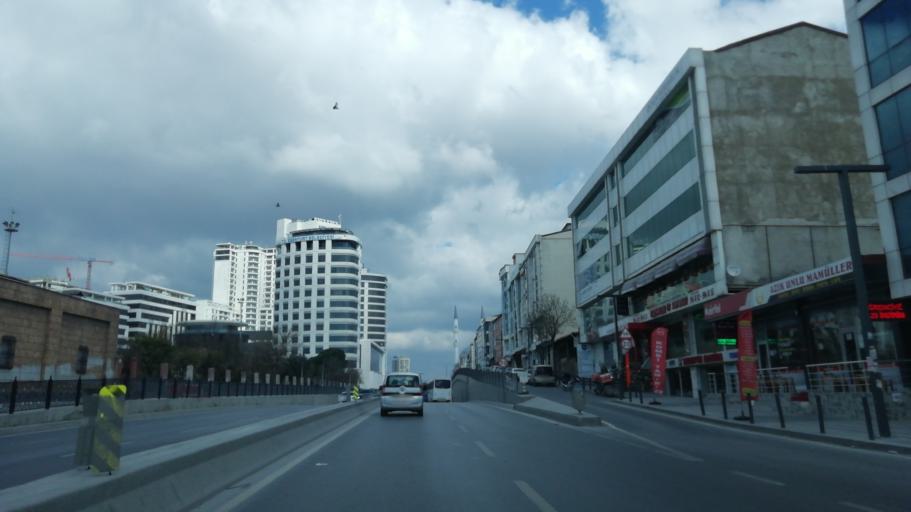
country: TR
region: Istanbul
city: Esenyurt
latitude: 41.0175
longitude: 28.6898
